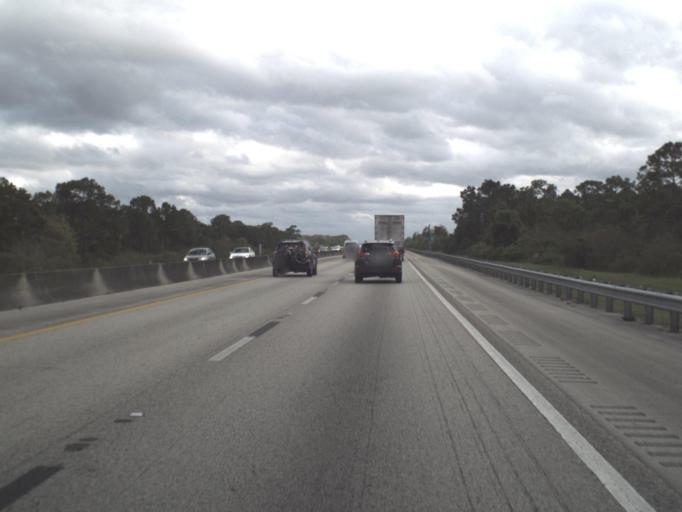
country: US
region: Florida
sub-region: Palm Beach County
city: Limestone Creek
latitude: 26.9669
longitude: -80.1748
